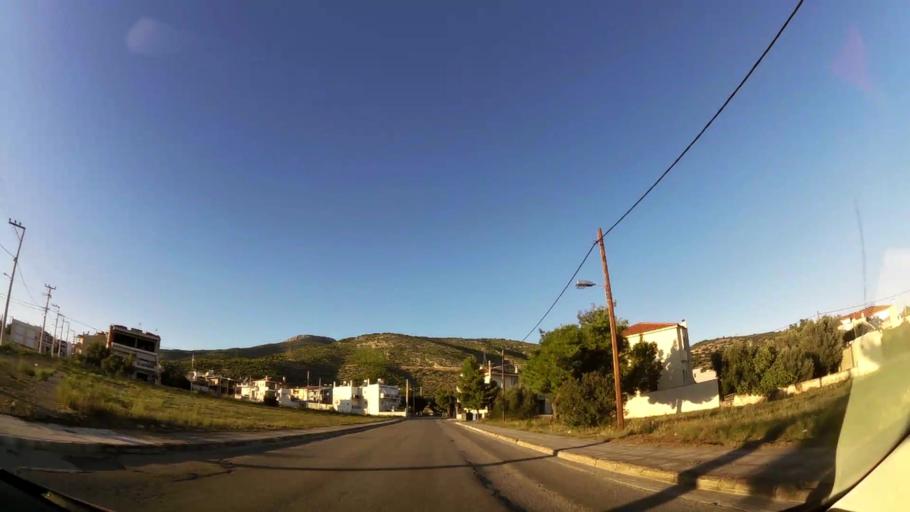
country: GR
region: Attica
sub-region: Nomarchia Dytikis Attikis
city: Ano Liosia
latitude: 38.0922
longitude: 23.7001
